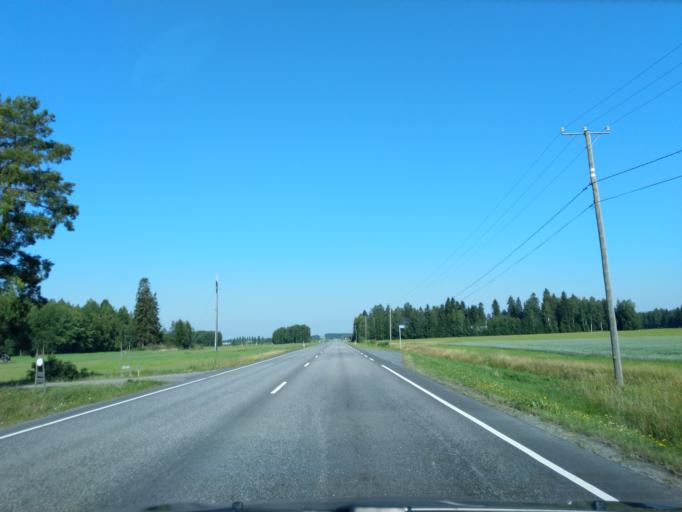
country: FI
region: Pirkanmaa
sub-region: Lounais-Pirkanmaa
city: Punkalaidun
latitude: 61.0313
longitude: 23.0225
